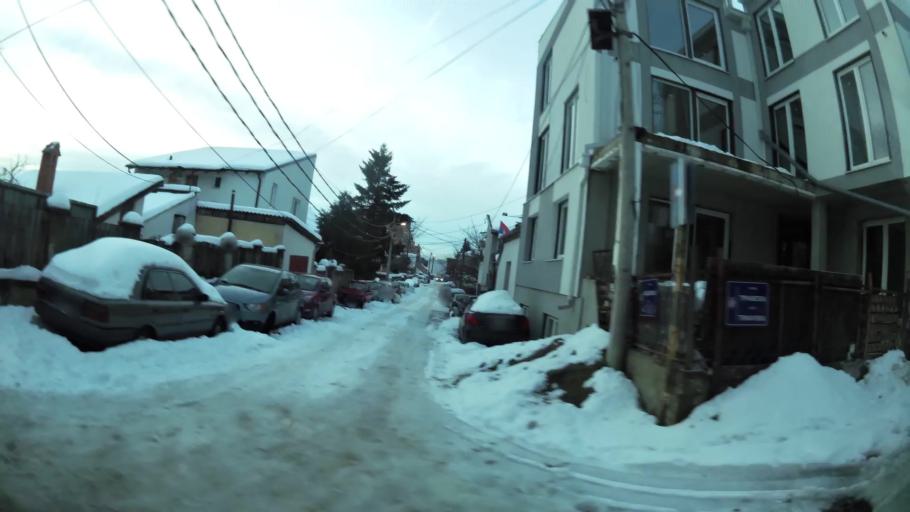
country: RS
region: Central Serbia
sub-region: Belgrade
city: Palilula
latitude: 44.8018
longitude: 20.5024
